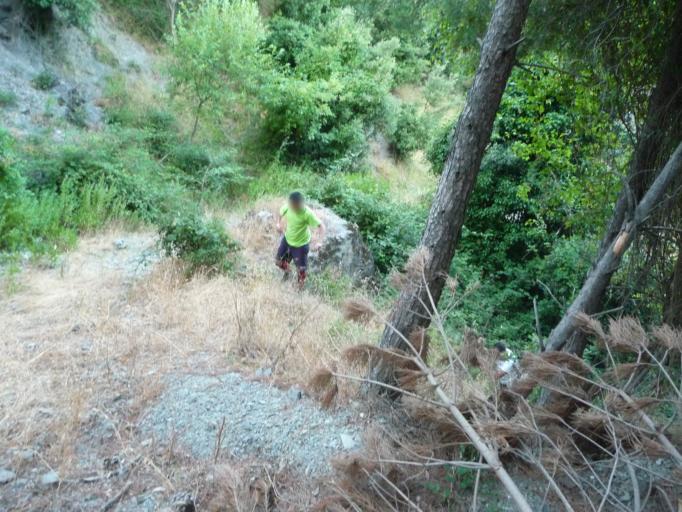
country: IT
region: Calabria
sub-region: Provincia di Reggio Calabria
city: Pazzano
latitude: 38.4641
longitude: 16.4285
